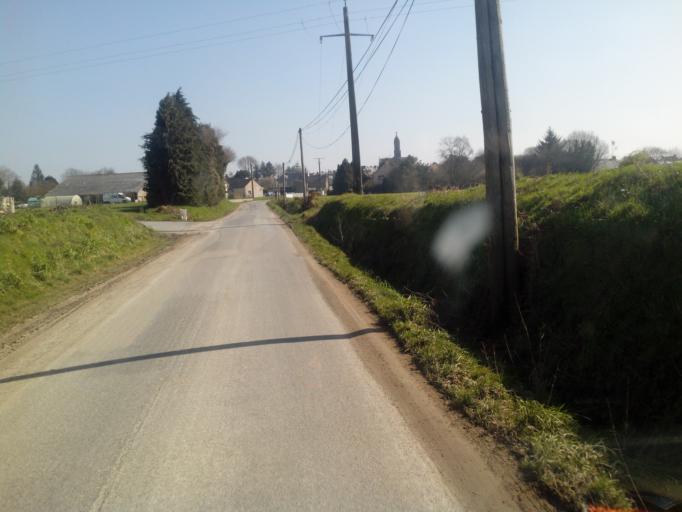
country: FR
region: Brittany
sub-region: Departement du Morbihan
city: Meneac
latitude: 48.1397
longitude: -2.4682
